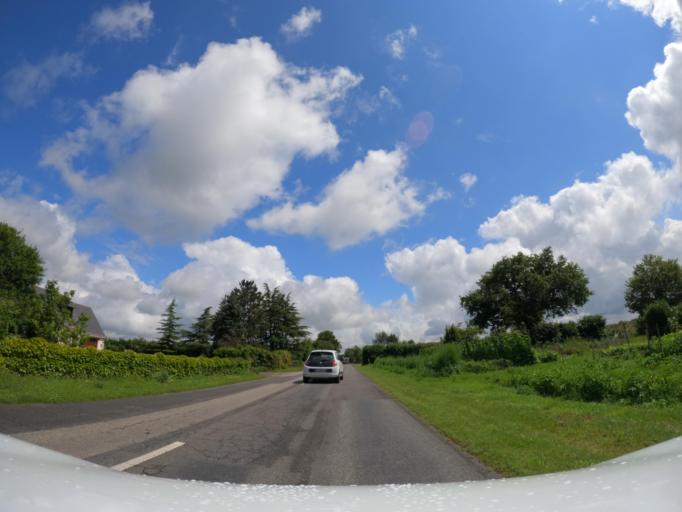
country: FR
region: Pays de la Loire
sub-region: Departement de la Loire-Atlantique
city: Saint-Mars-du-Desert
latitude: 47.3812
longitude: -1.3944
